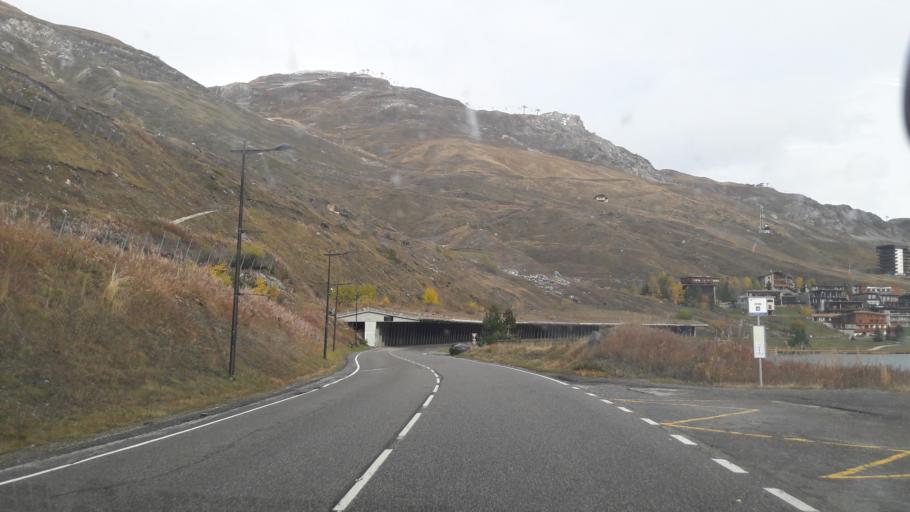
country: FR
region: Rhone-Alpes
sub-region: Departement de la Savoie
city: Tignes
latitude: 45.4635
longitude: 6.8988
